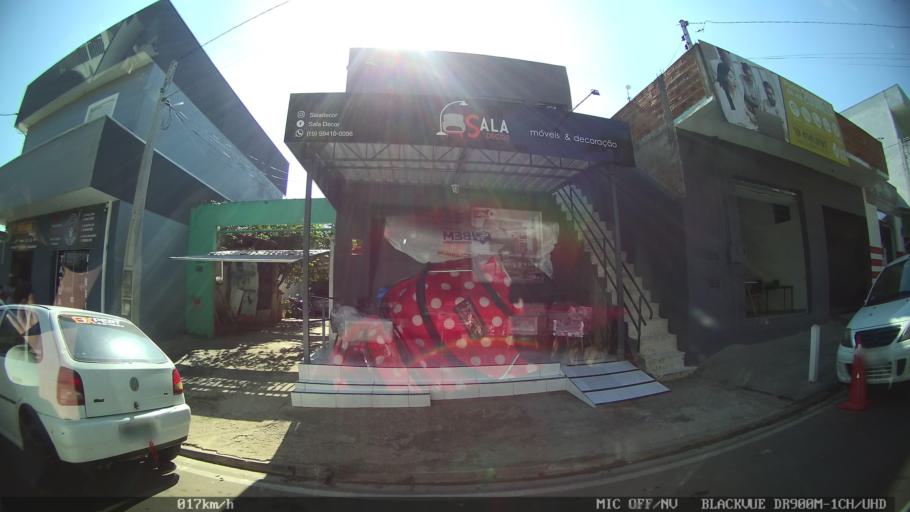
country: BR
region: Sao Paulo
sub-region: Campinas
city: Campinas
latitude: -22.9386
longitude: -47.0791
